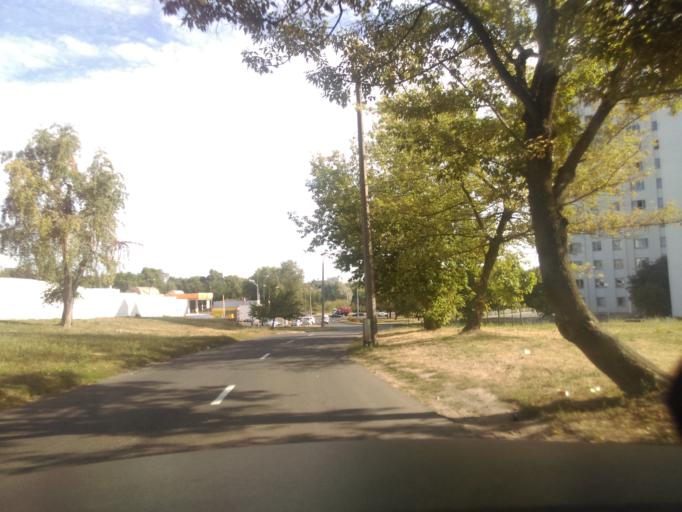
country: BY
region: Minsk
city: Minsk
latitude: 53.8799
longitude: 27.5971
